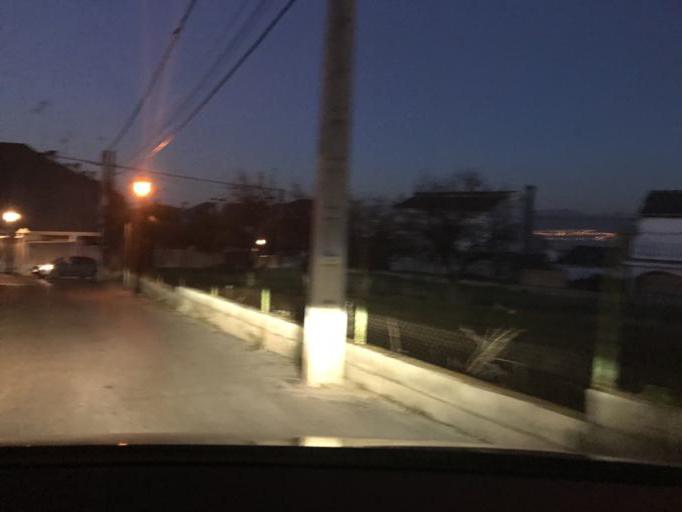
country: ES
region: Andalusia
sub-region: Provincia de Granada
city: Ogijares
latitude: 37.1134
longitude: -3.6153
